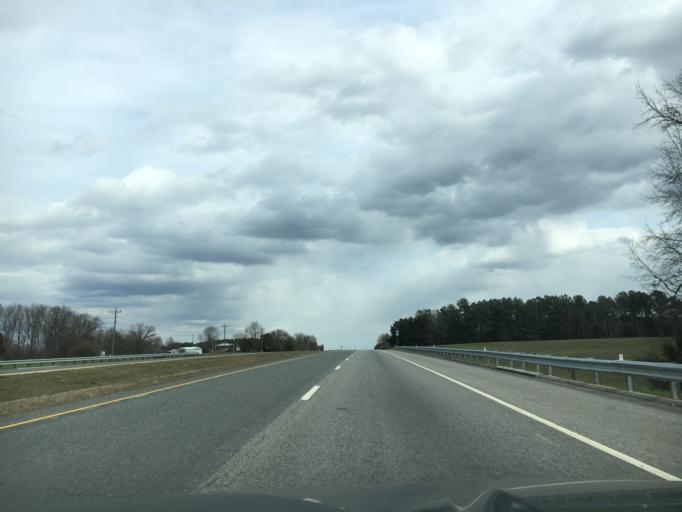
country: US
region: Virginia
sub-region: Mecklenburg County
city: Boydton
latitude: 36.6713
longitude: -78.2637
